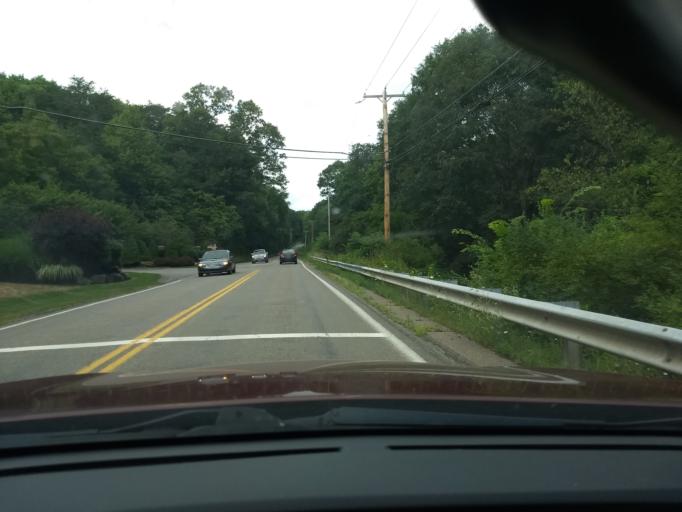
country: US
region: Pennsylvania
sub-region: Butler County
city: Cranberry Township
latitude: 40.6460
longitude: -80.1253
